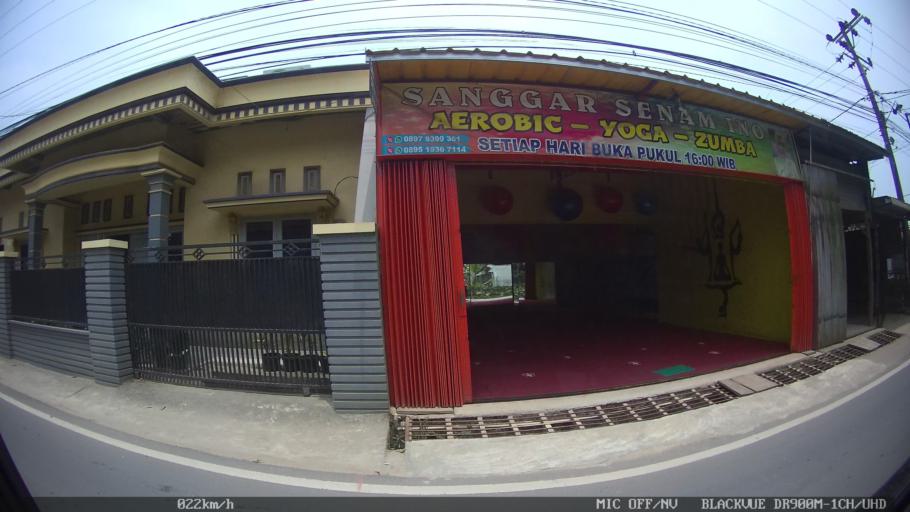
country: ID
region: Lampung
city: Kedaton
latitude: -5.3995
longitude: 105.3167
